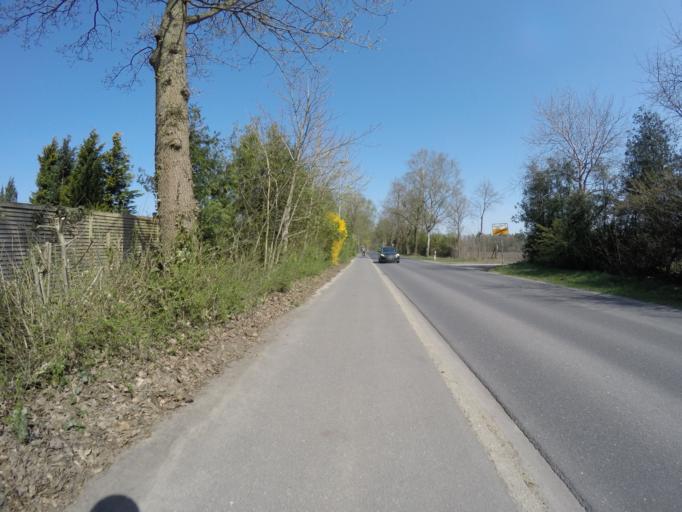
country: DE
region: Schleswig-Holstein
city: Quickborn
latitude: 53.7277
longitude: 9.9301
